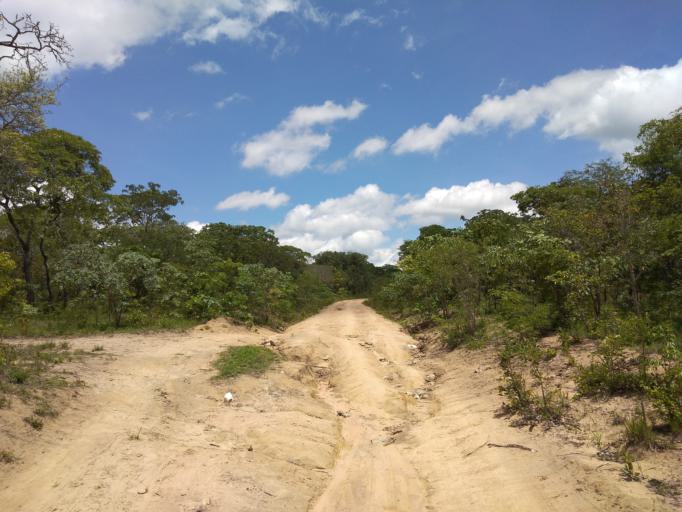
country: ZM
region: Central
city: Mkushi
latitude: -13.9578
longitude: 29.9194
